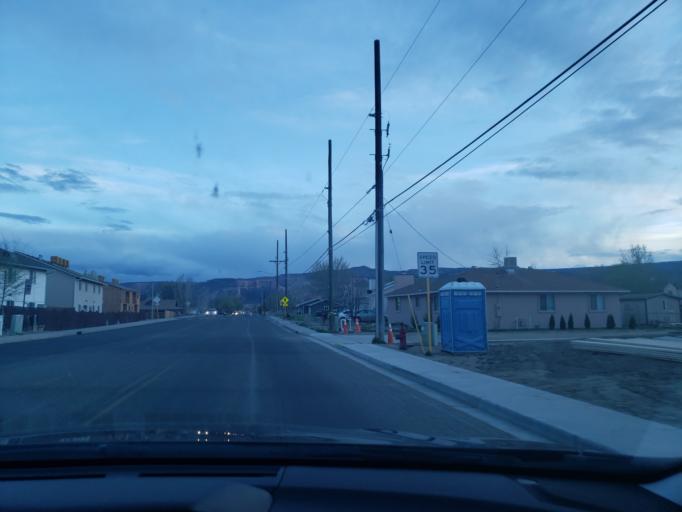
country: US
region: Colorado
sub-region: Mesa County
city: Fruita
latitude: 39.1574
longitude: -108.7198
